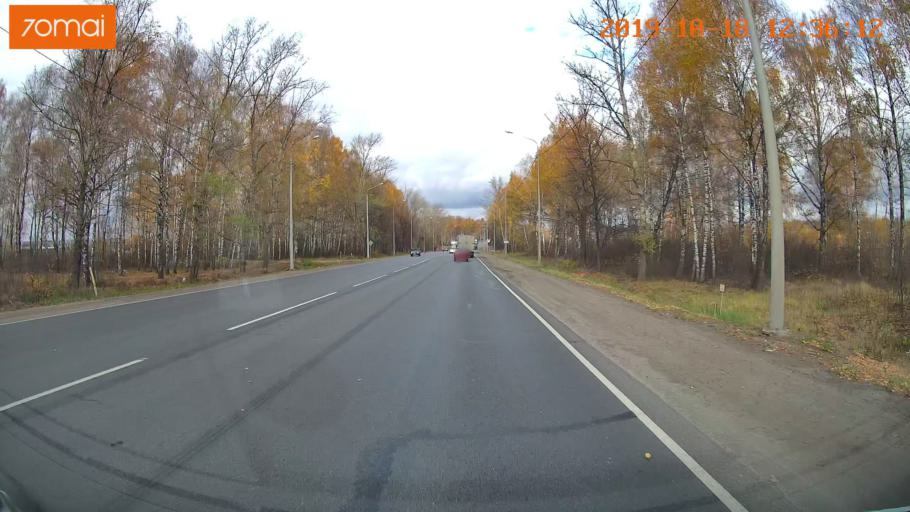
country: RU
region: Rjazan
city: Ryazan'
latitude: 54.6327
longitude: 39.6343
